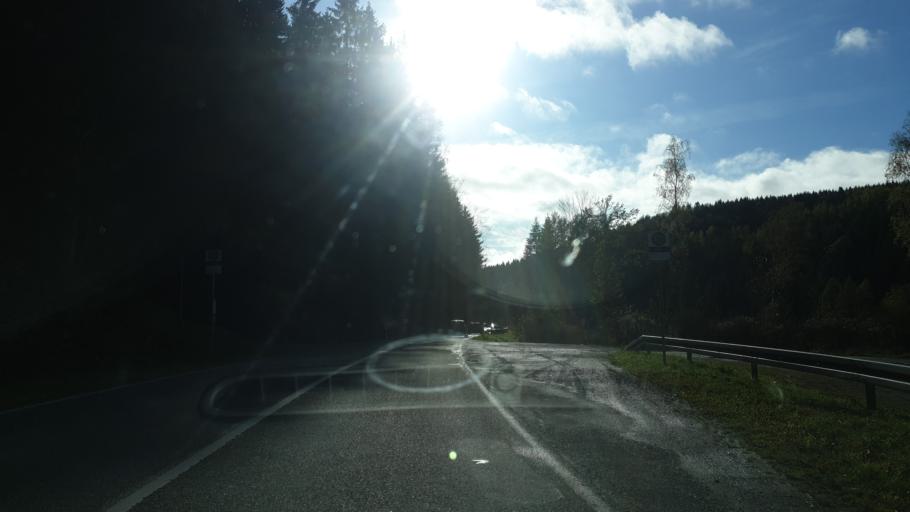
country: DE
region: Saxony
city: Bockau
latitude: 50.5648
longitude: 12.6923
